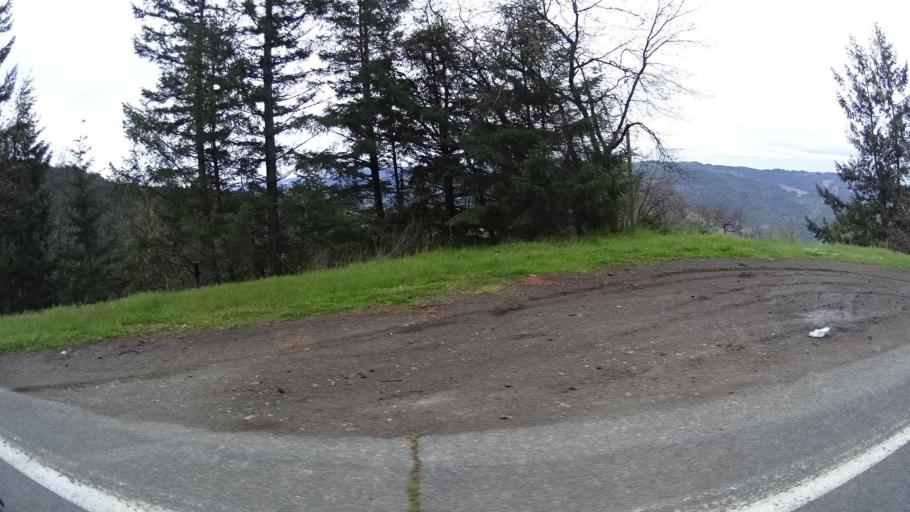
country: US
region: California
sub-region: Humboldt County
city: Willow Creek
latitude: 40.8803
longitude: -123.7648
